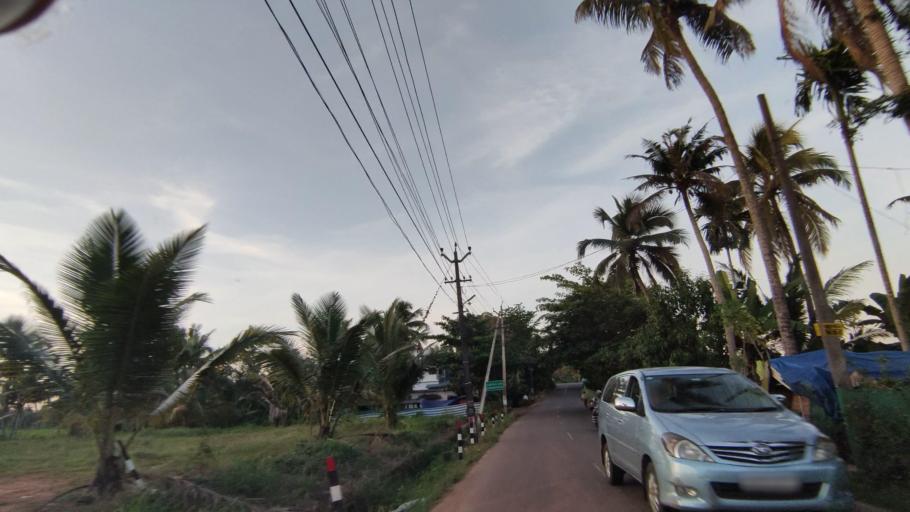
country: IN
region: Kerala
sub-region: Kottayam
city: Kottayam
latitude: 9.6451
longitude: 76.5093
